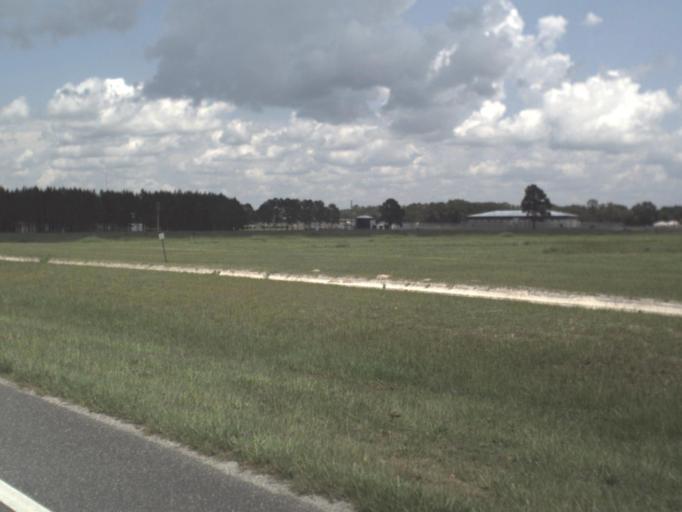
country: US
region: Florida
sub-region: Gilchrist County
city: Trenton
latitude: 29.6127
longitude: -82.8711
